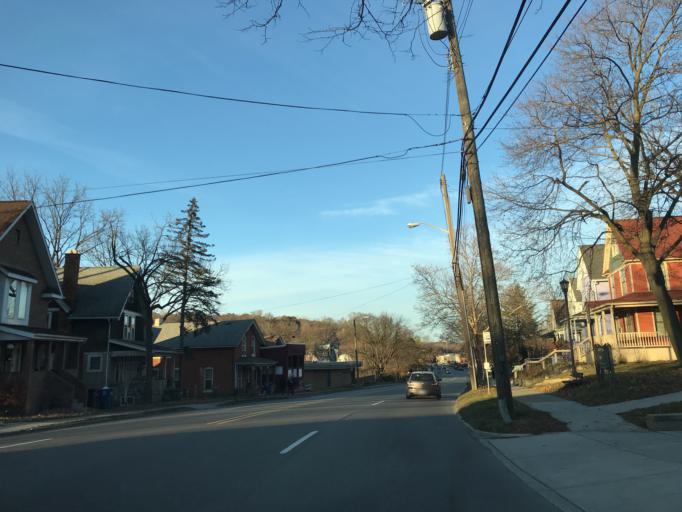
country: US
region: Michigan
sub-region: Washtenaw County
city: Ann Arbor
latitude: 42.2862
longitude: -83.7482
